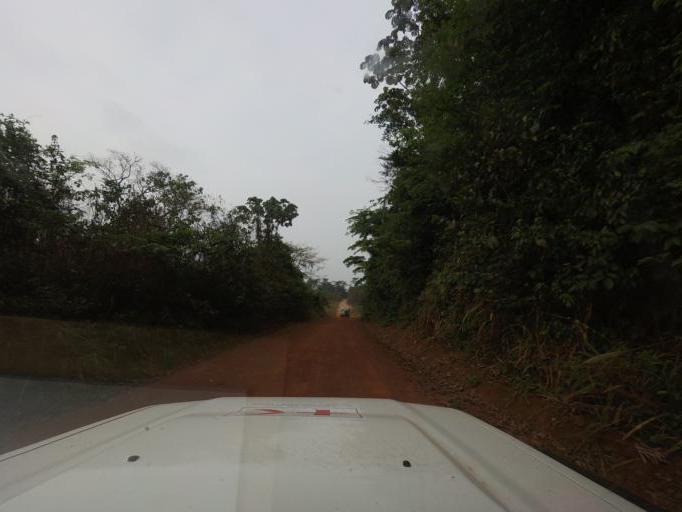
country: LR
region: Lofa
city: Voinjama
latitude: 8.3911
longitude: -9.8111
